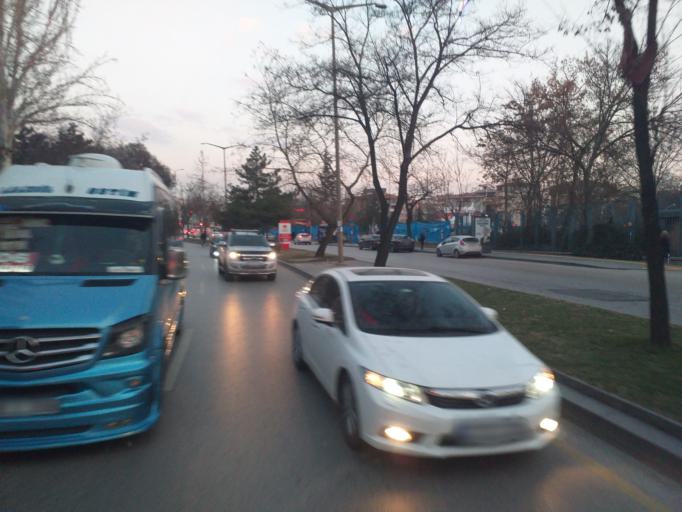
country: TR
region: Ankara
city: Ankara
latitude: 39.9340
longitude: 32.8271
